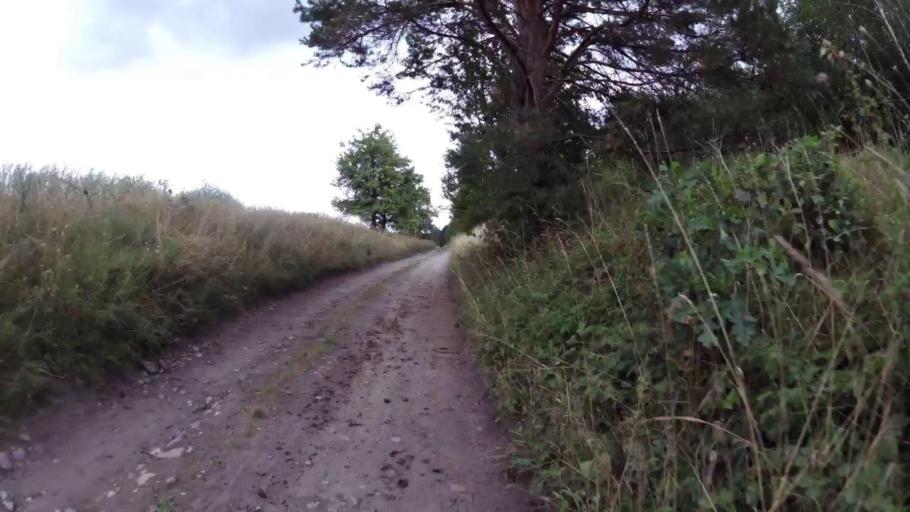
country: PL
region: West Pomeranian Voivodeship
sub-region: Powiat mysliborski
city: Debno
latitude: 52.7789
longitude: 14.7098
